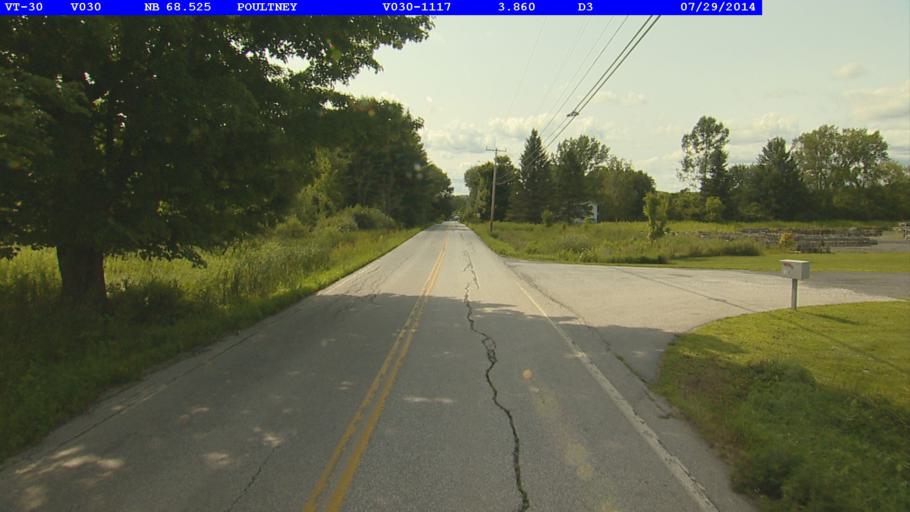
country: US
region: Vermont
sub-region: Rutland County
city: Poultney
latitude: 43.5128
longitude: -73.2224
